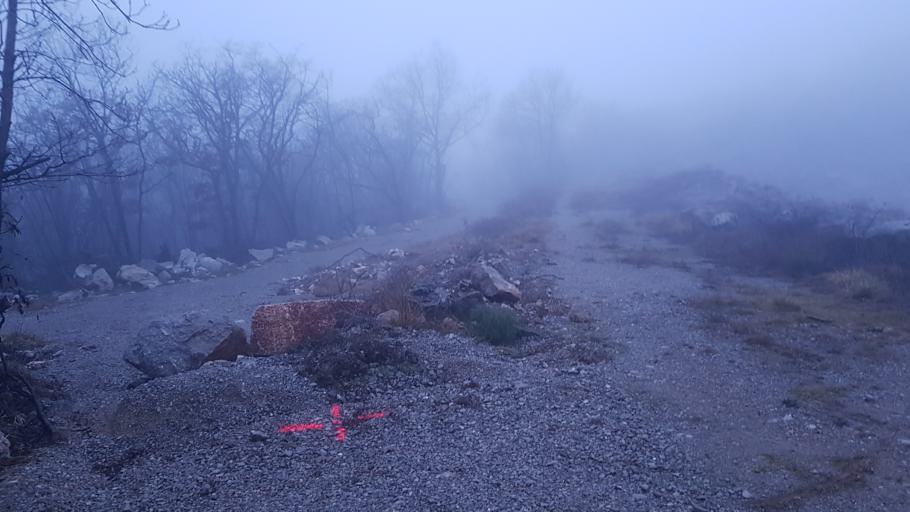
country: IT
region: Friuli Venezia Giulia
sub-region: Provincia di Trieste
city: Zolla
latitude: 45.7147
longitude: 13.8410
